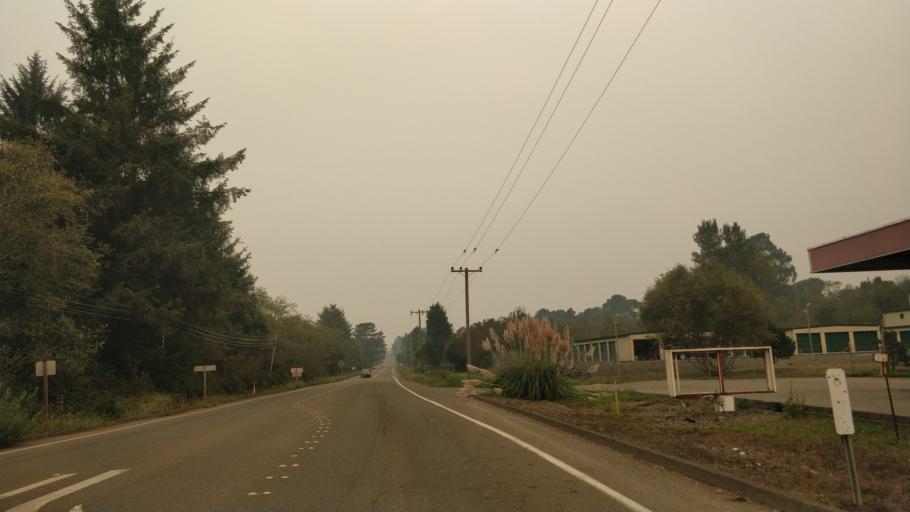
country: US
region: California
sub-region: Humboldt County
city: McKinleyville
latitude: 40.9563
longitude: -124.1008
